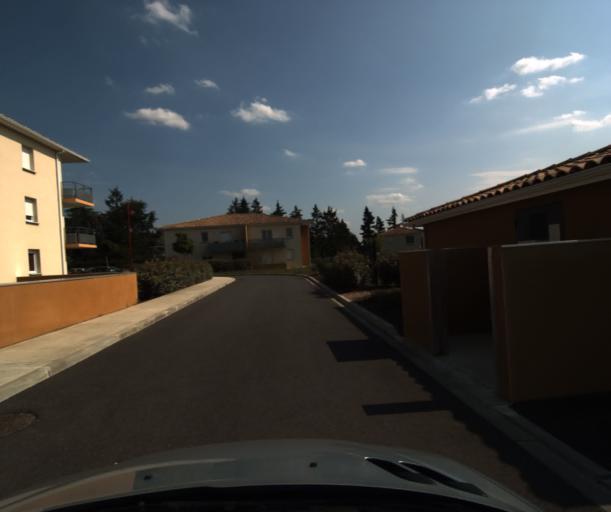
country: FR
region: Midi-Pyrenees
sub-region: Departement de la Haute-Garonne
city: Saint-Lys
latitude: 43.5214
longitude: 1.1874
